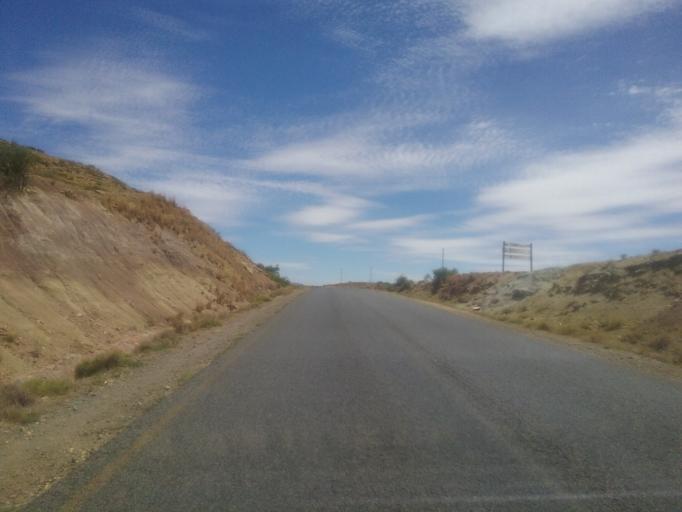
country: LS
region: Mohale's Hoek District
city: Mohale's Hoek
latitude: -30.0662
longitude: 27.4205
